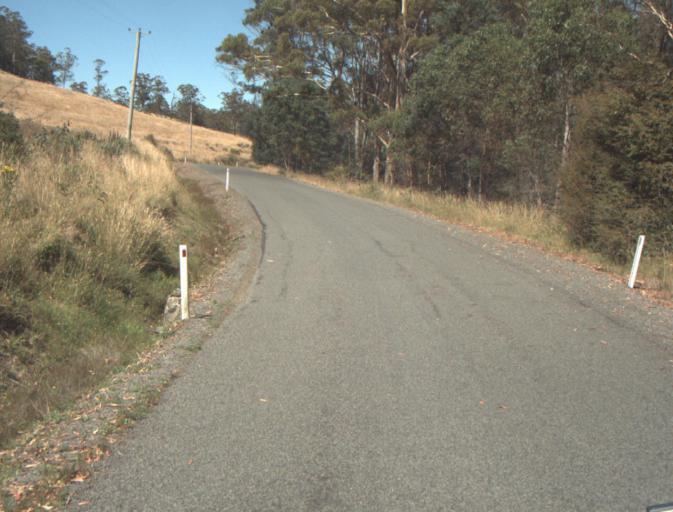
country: AU
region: Tasmania
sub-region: Launceston
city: Newstead
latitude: -41.3564
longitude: 147.3029
